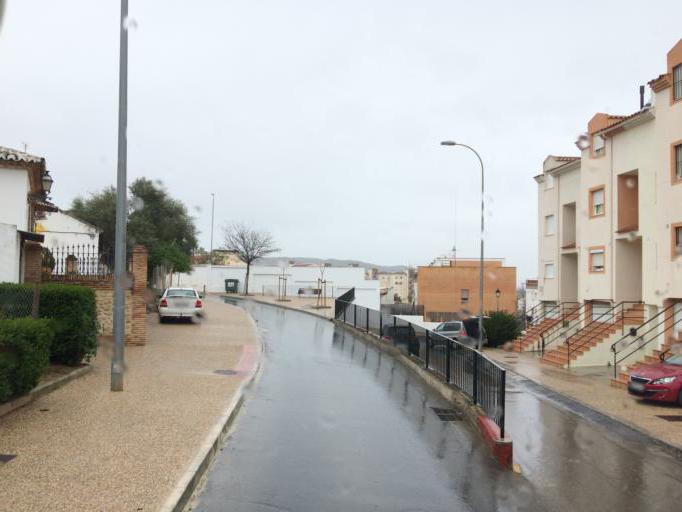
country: ES
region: Andalusia
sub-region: Provincia de Malaga
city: Antequera
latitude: 37.0266
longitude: -4.5568
